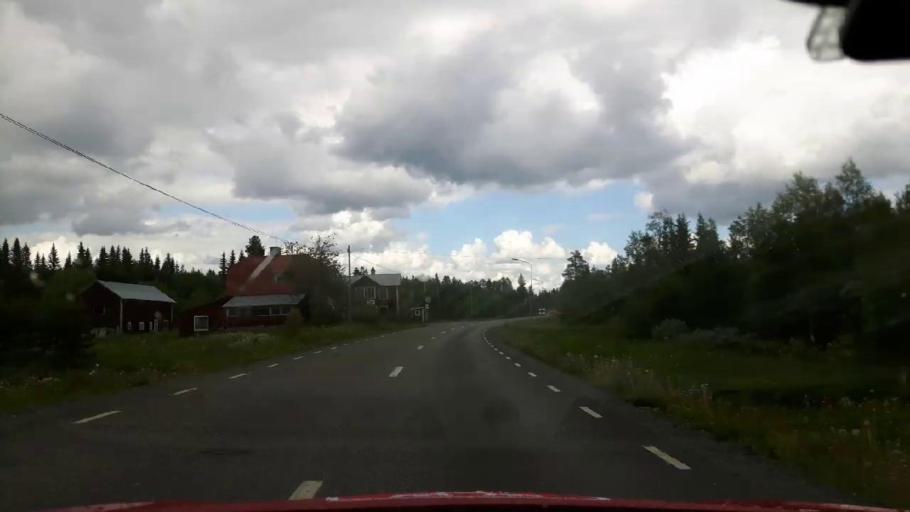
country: SE
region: Jaemtland
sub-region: Krokoms Kommun
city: Krokom
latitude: 63.7487
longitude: 14.2906
